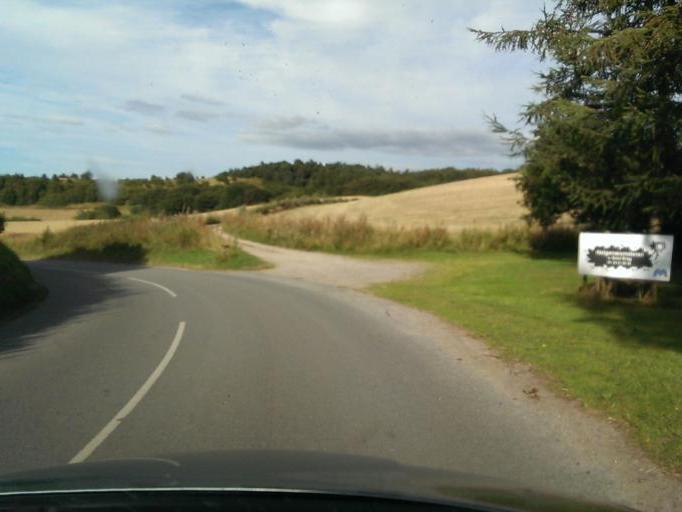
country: DK
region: Central Jutland
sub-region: Syddjurs Kommune
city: Ronde
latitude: 56.1329
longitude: 10.5135
